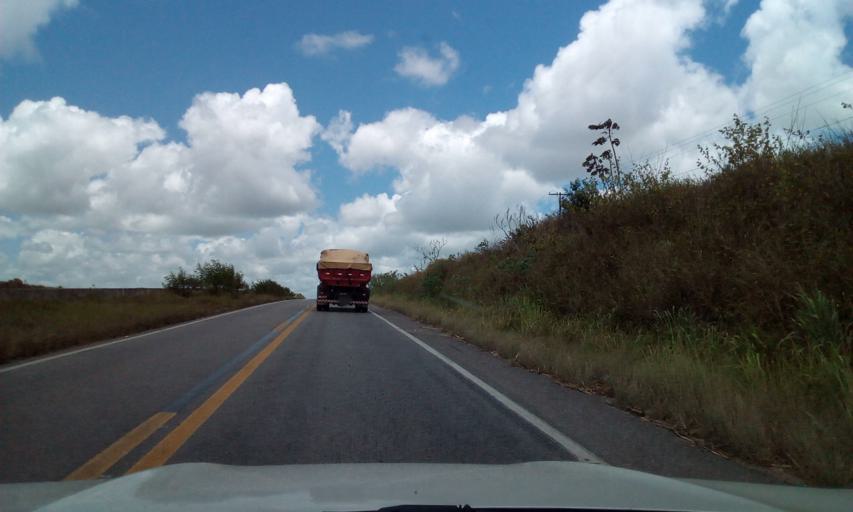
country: BR
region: Alagoas
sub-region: Sao Miguel Dos Campos
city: Sao Miguel dos Campos
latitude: -9.8262
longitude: -36.1268
